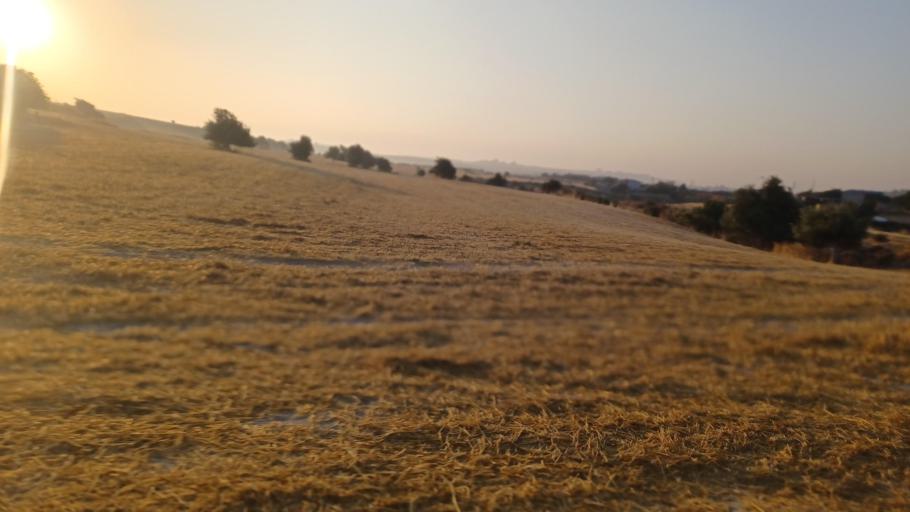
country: CY
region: Larnaka
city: Tersefanou
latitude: 34.9002
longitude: 33.5150
